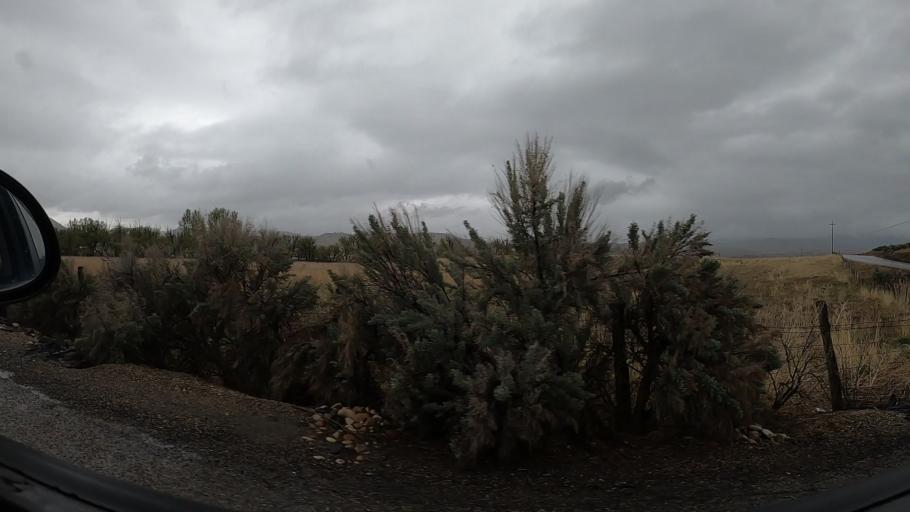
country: US
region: Idaho
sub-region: Ada County
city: Eagle
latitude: 43.7292
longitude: -116.2819
